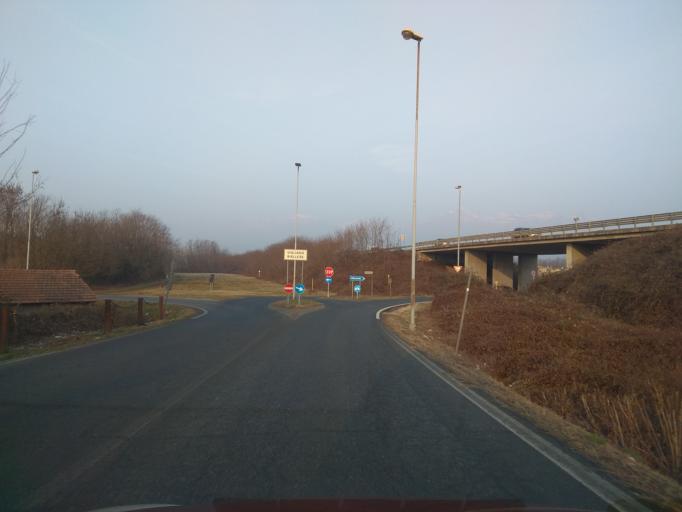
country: IT
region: Piedmont
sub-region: Provincia di Biella
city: Vigliano Biellese
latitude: 45.5551
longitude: 8.1122
